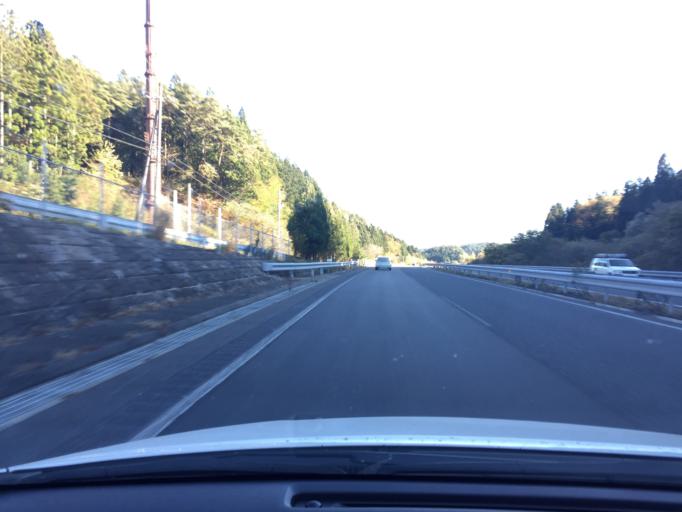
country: JP
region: Fukushima
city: Iwaki
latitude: 37.1943
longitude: 140.7047
